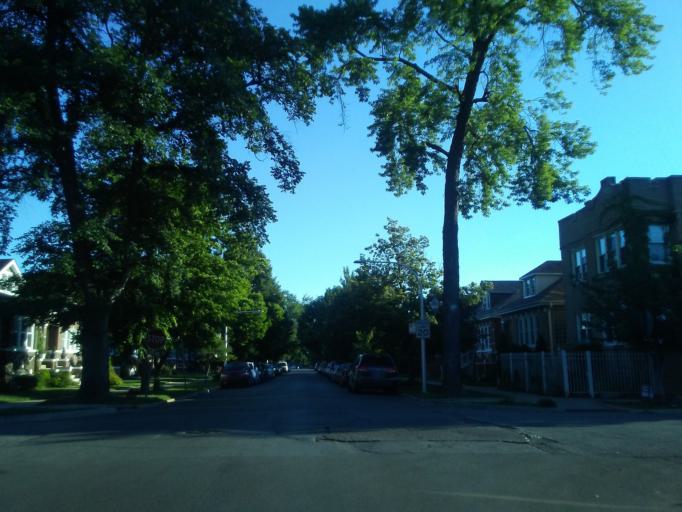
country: US
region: Illinois
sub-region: Cook County
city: Lincolnwood
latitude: 41.9371
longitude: -87.7369
